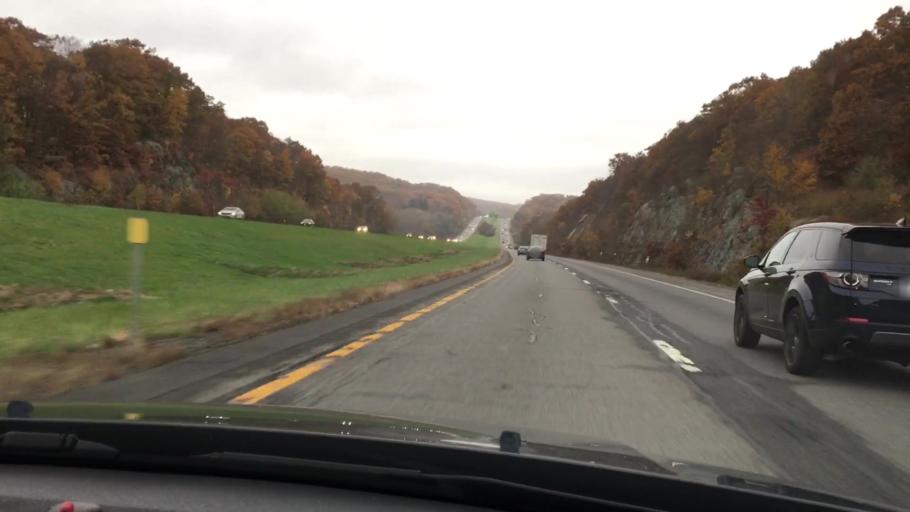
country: US
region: New York
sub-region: Putnam County
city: Brewster Hill
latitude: 41.4430
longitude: -73.6331
